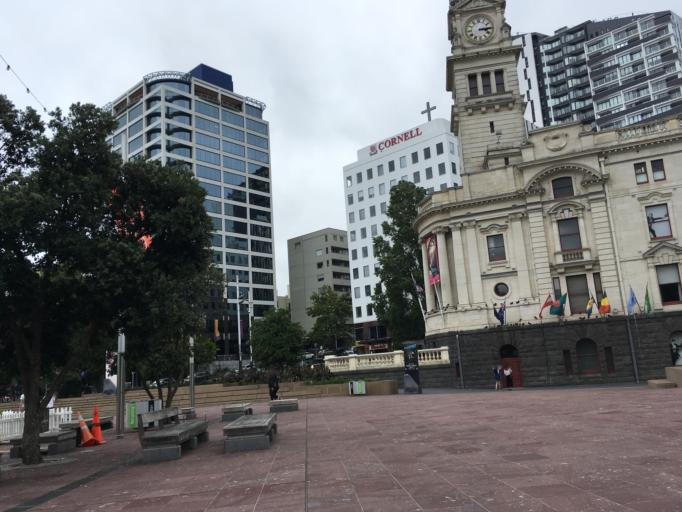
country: NZ
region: Auckland
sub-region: Auckland
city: Auckland
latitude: -36.8522
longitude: 174.7631
